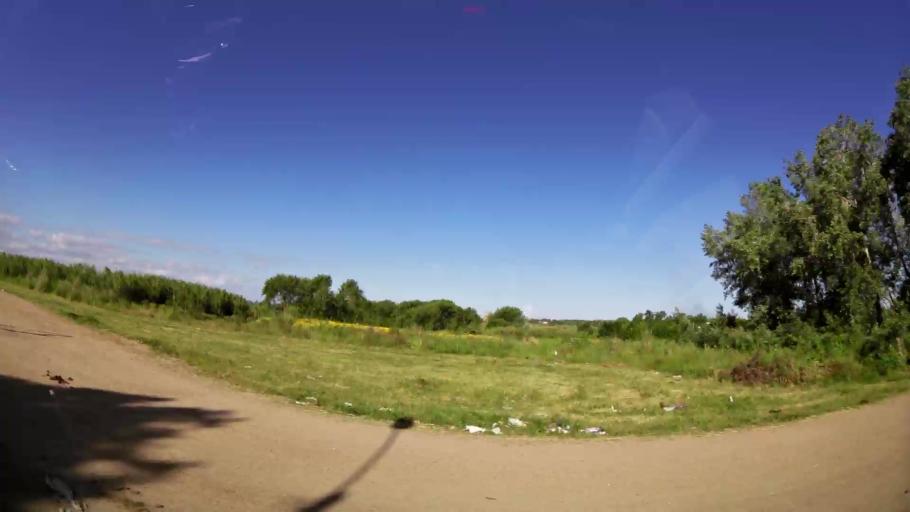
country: UY
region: Canelones
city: La Paz
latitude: -34.8132
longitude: -56.1588
